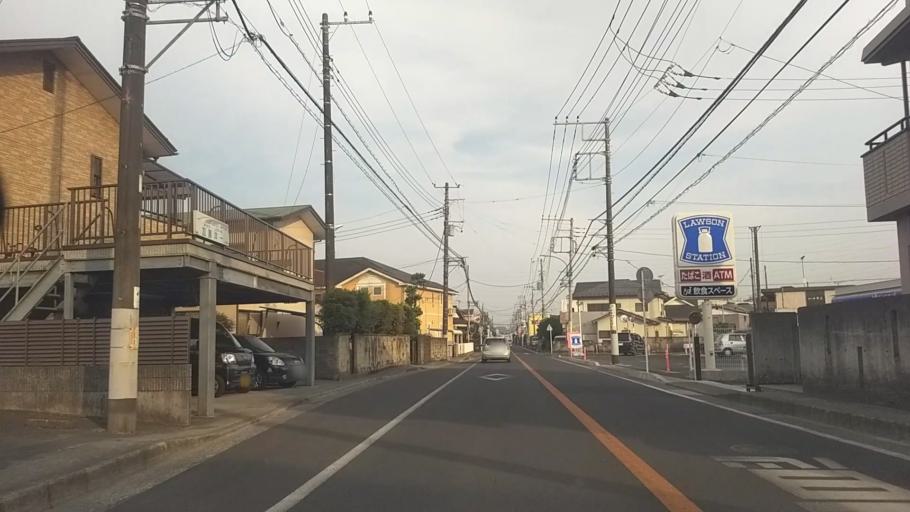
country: JP
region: Kanagawa
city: Odawara
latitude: 35.2988
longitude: 139.1282
